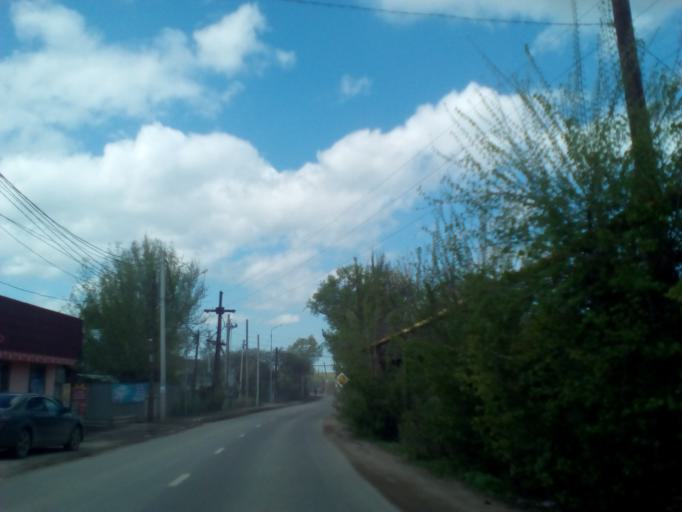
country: KZ
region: Almaty Oblysy
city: Burunday
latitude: 43.2458
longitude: 76.7505
